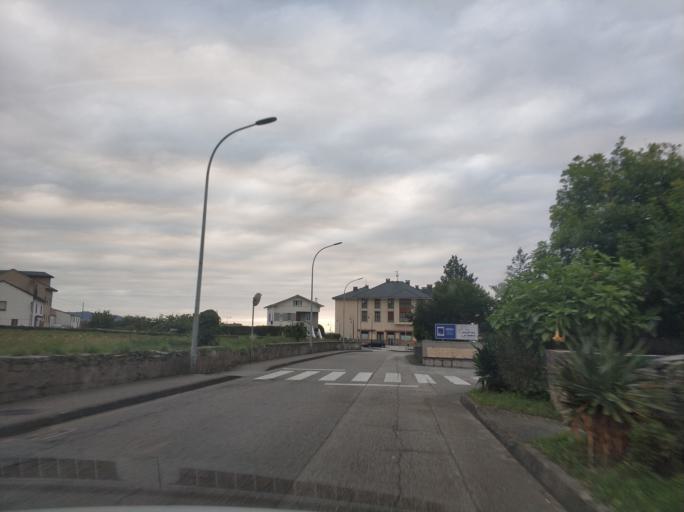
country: ES
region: Asturias
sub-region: Province of Asturias
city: Navia
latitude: 43.5448
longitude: -6.5286
